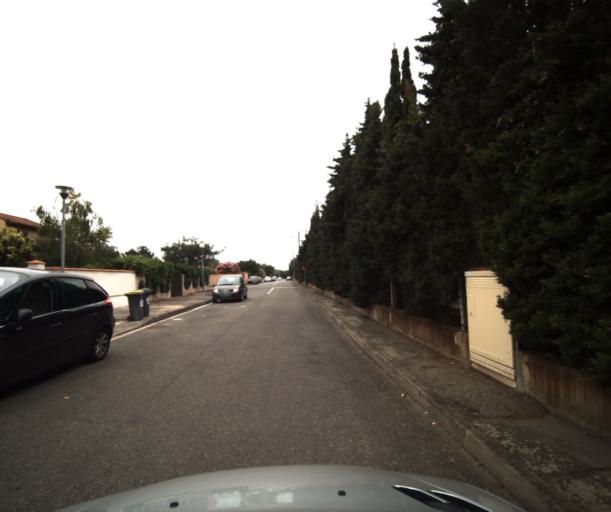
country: FR
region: Midi-Pyrenees
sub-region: Departement de la Haute-Garonne
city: Portet-sur-Garonne
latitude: 43.5430
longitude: 1.4047
